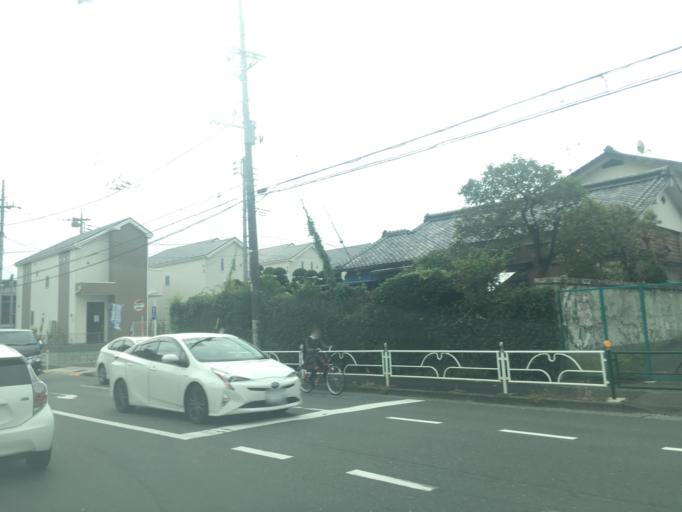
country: JP
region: Tokyo
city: Higashimurayama-shi
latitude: 35.7302
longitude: 139.4650
